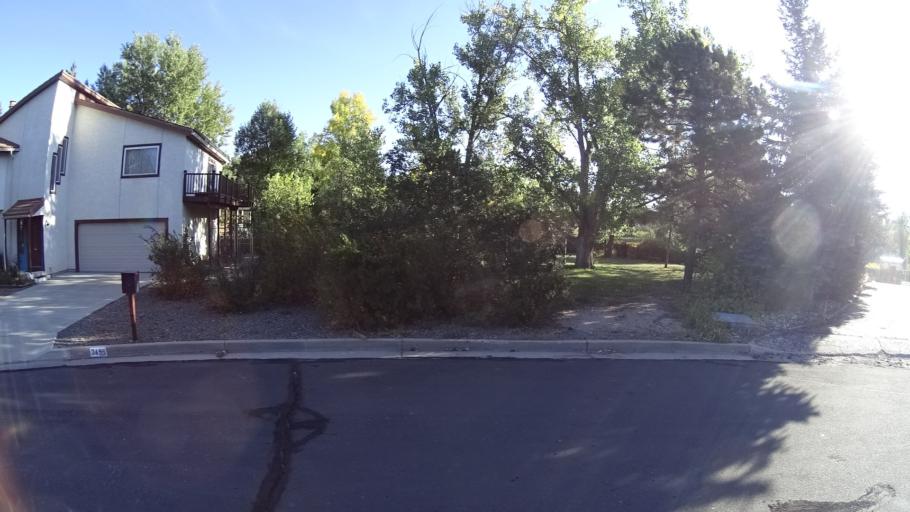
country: US
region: Colorado
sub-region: El Paso County
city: Cimarron Hills
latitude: 38.8818
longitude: -104.7653
